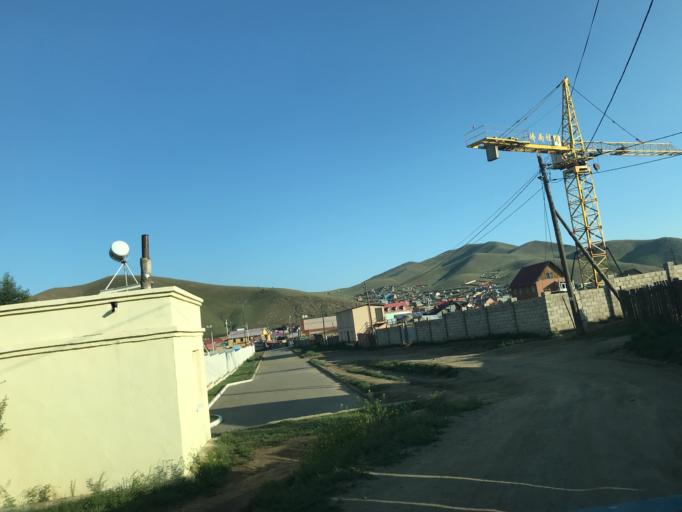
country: MN
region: Ulaanbaatar
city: Ulaanbaatar
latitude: 47.9949
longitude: 106.9686
